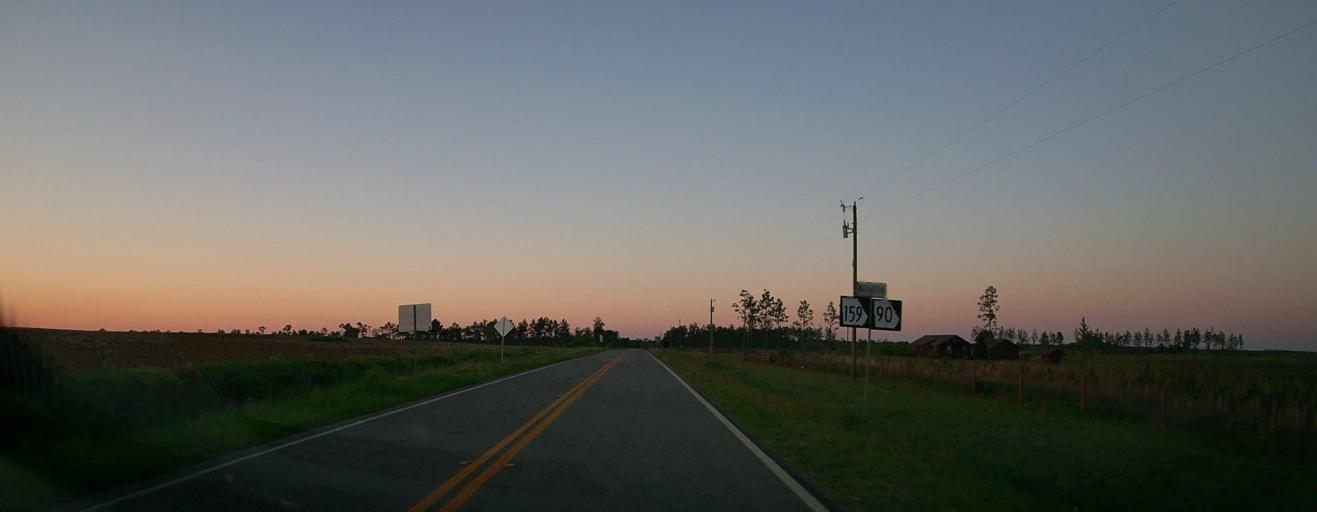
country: US
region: Georgia
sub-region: Turner County
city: Ashburn
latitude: 31.8244
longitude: -83.5650
